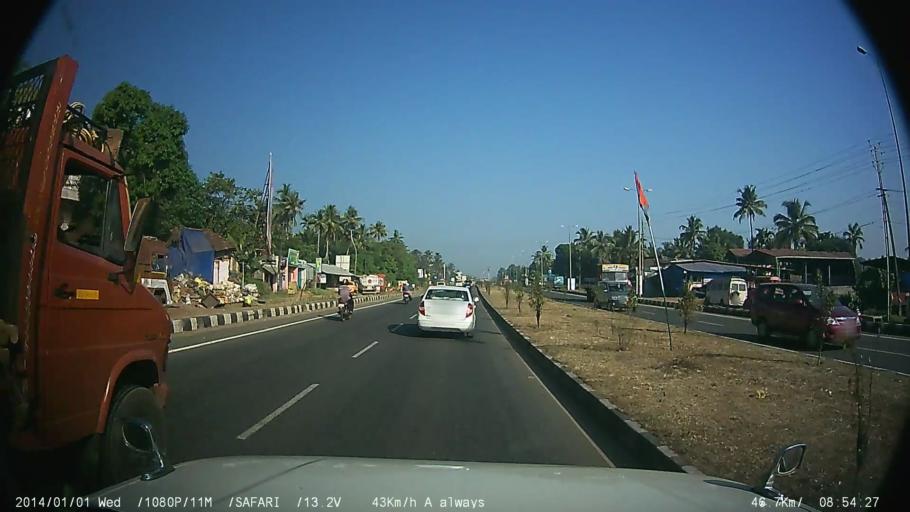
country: IN
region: Kerala
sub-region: Ernakulam
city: Angamali
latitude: 10.2173
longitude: 76.3778
